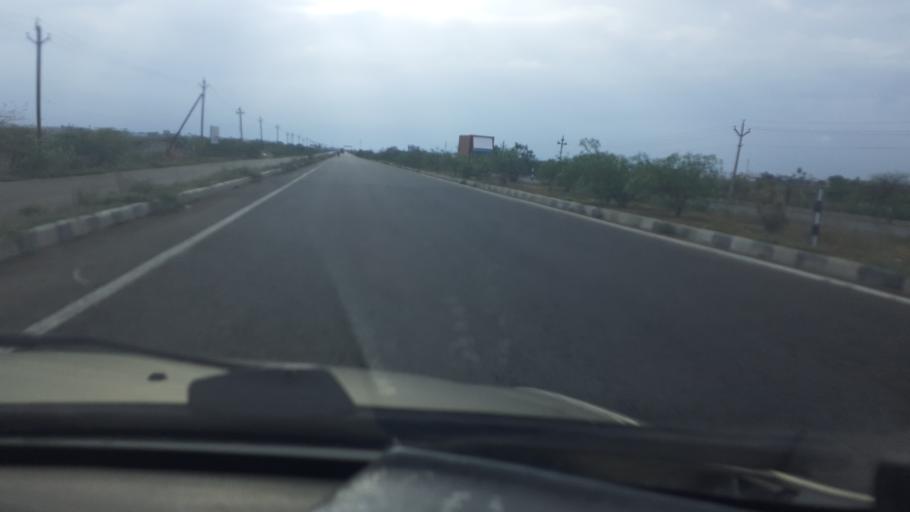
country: IN
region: Tamil Nadu
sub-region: Tirunelveli Kattabo
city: Tirunelveli
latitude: 8.6646
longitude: 77.7323
